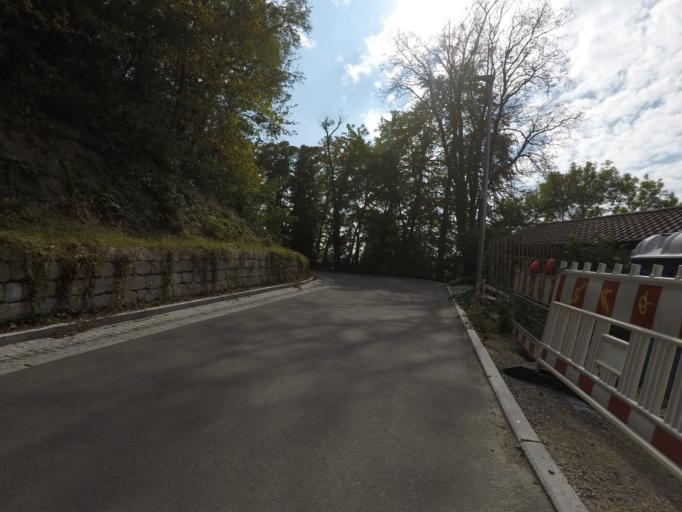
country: DE
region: Baden-Wuerttemberg
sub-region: Tuebingen Region
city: Reutlingen
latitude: 48.4943
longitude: 9.2276
